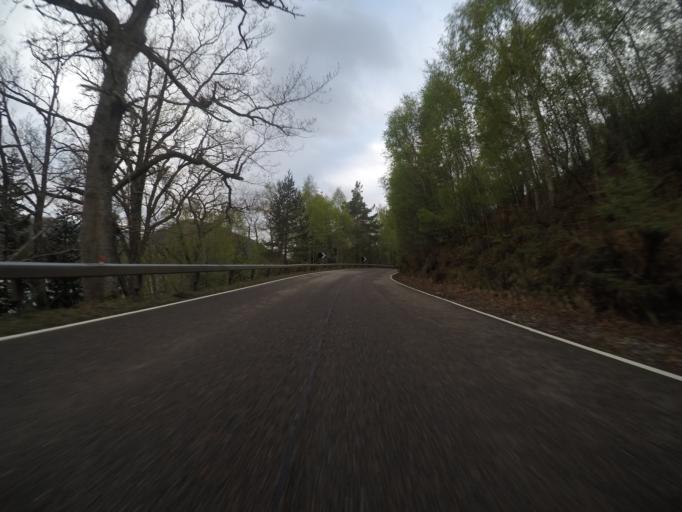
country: GB
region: Scotland
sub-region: Highland
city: Kingussie
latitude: 56.9612
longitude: -4.4580
